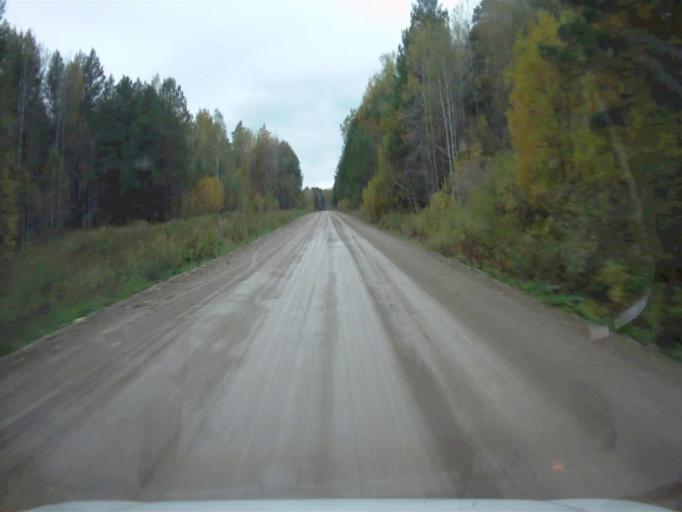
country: RU
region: Chelyabinsk
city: Nyazepetrovsk
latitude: 56.0940
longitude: 59.4053
